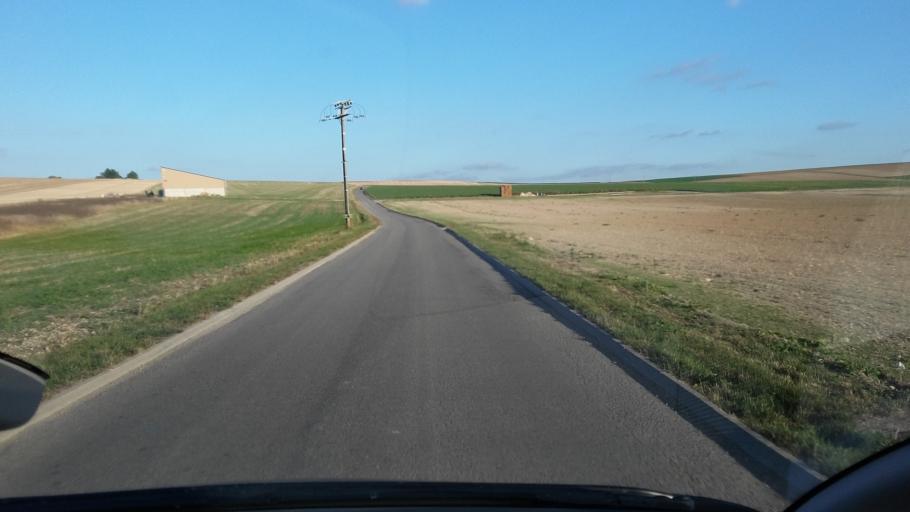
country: FR
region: Champagne-Ardenne
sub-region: Departement de la Marne
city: Cormontreuil
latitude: 49.1969
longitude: 4.0193
